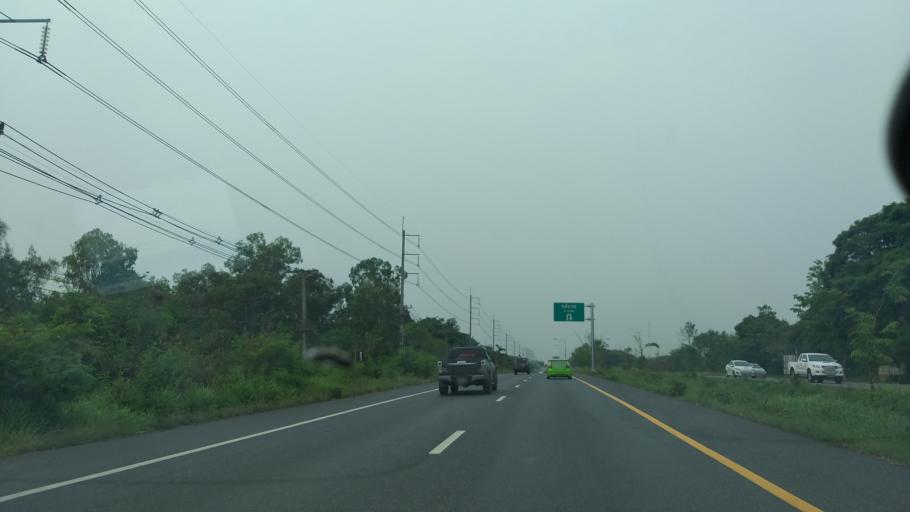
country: TH
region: Chon Buri
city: Ko Chan
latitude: 13.4135
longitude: 101.2822
